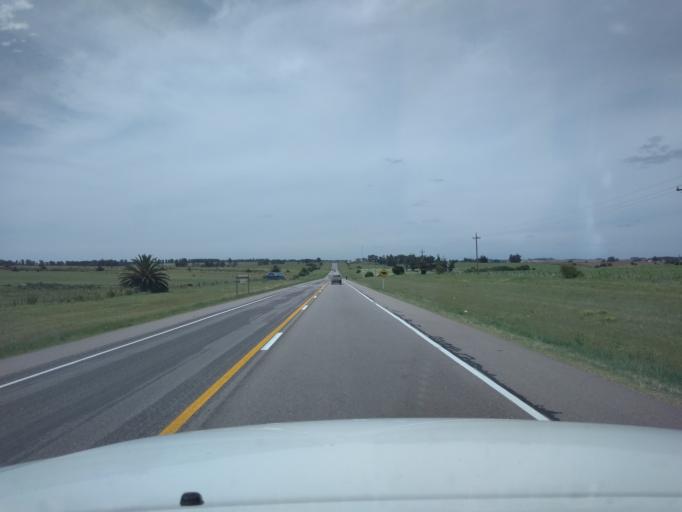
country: UY
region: Florida
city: Florida
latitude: -34.2252
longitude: -56.2106
